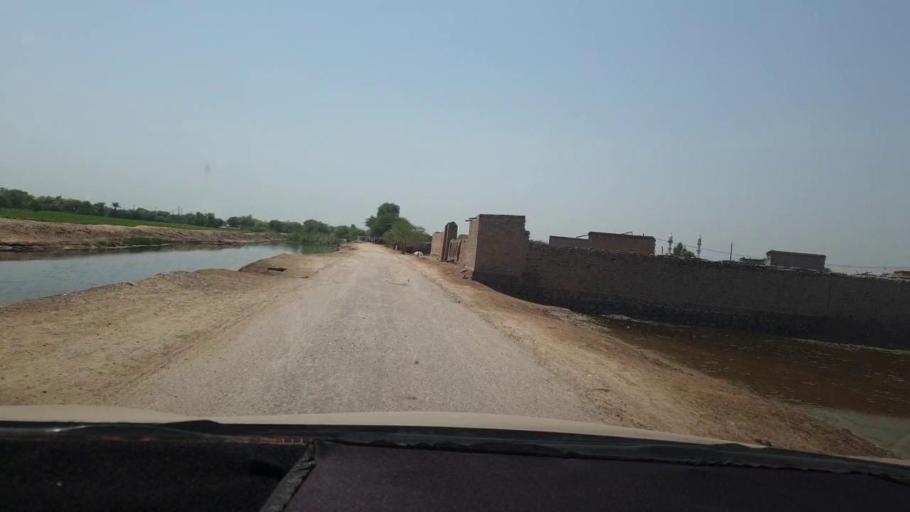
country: PK
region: Sindh
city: Shahdadkot
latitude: 27.8381
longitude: 67.9416
